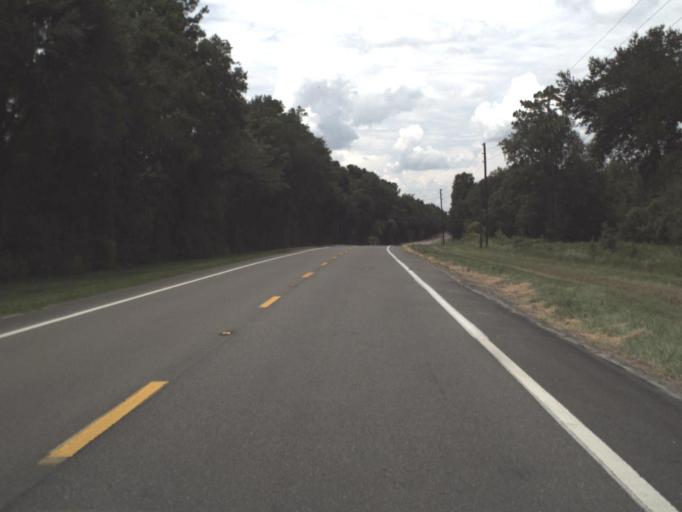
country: US
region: Florida
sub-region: Alachua County
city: Archer
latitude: 29.4861
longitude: -82.4912
